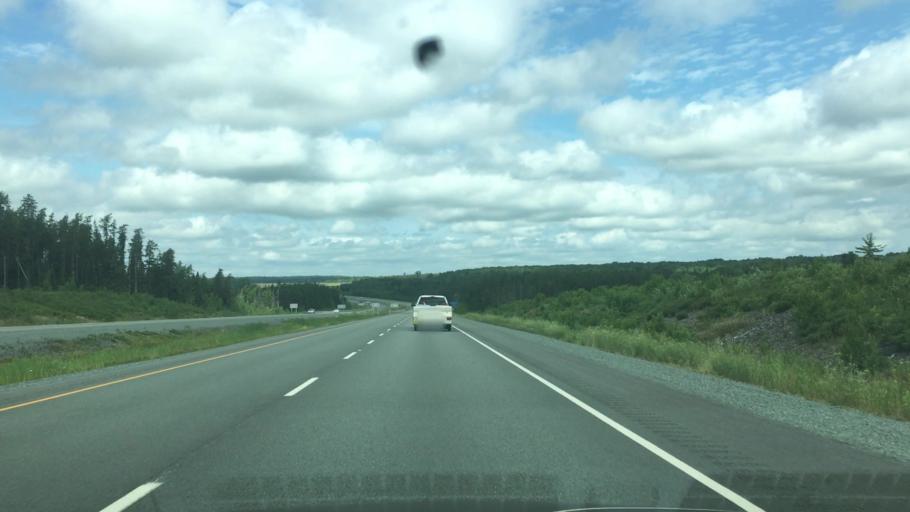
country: CA
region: Nova Scotia
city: Oxford
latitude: 45.6797
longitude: -63.7623
